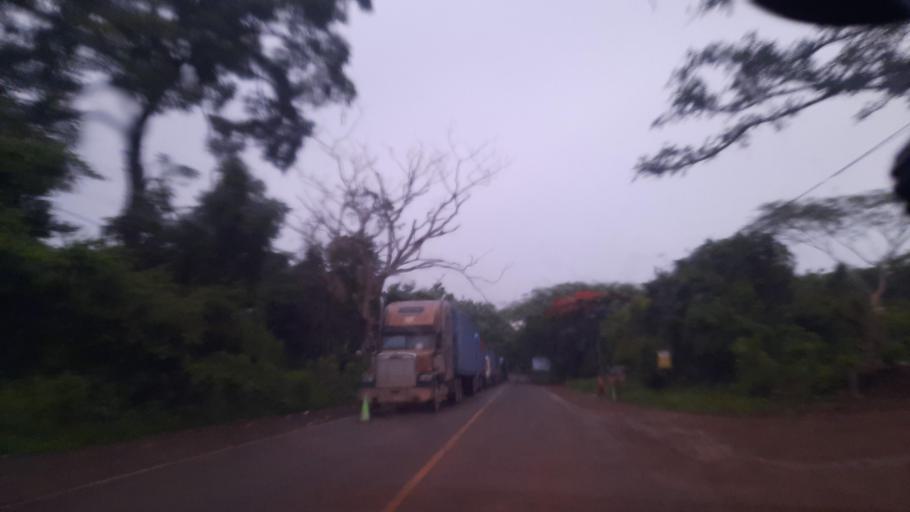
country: GT
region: Jutiapa
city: Atescatempa
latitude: 14.1961
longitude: -89.6753
